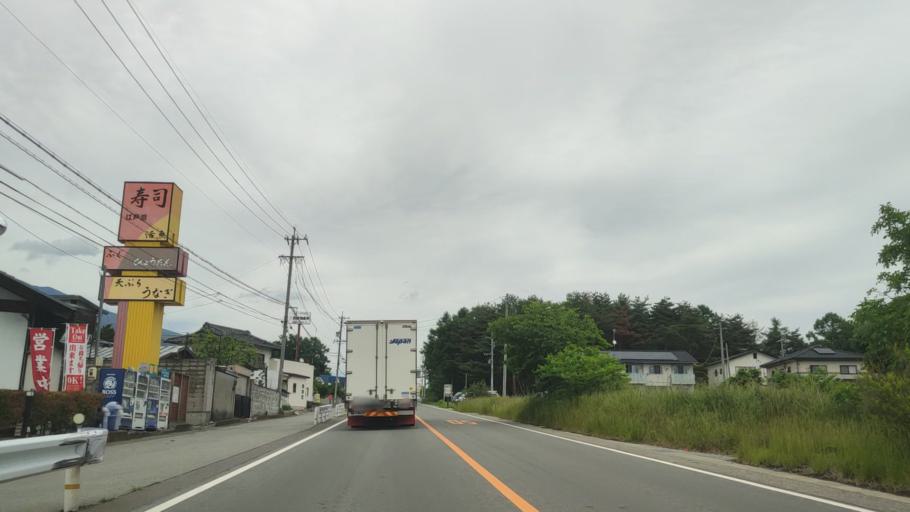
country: JP
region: Nagano
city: Komoro
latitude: 36.3222
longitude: 138.4992
